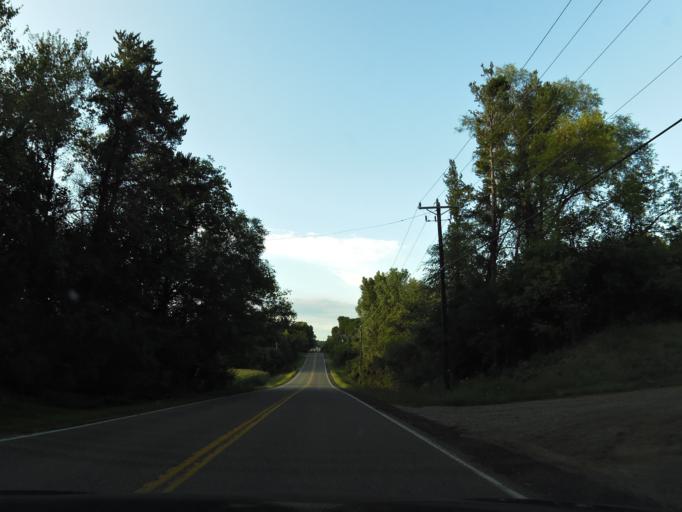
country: US
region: Minnesota
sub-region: Washington County
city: Lake Elmo
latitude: 44.9405
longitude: -92.8428
